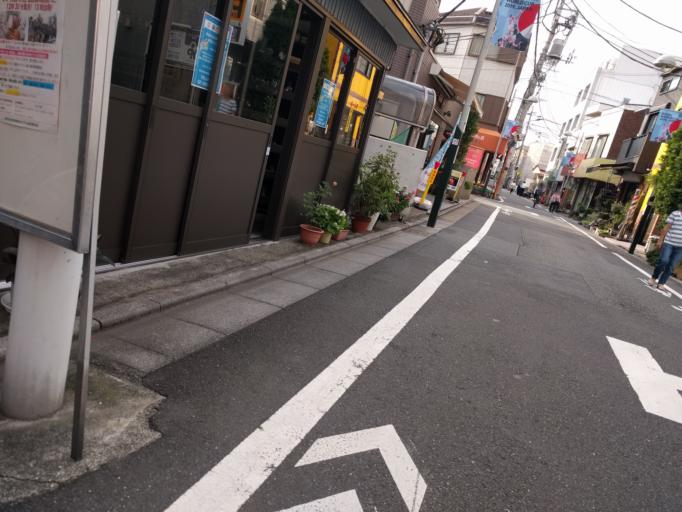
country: JP
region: Tokyo
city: Tokyo
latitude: 35.6532
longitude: 139.6351
